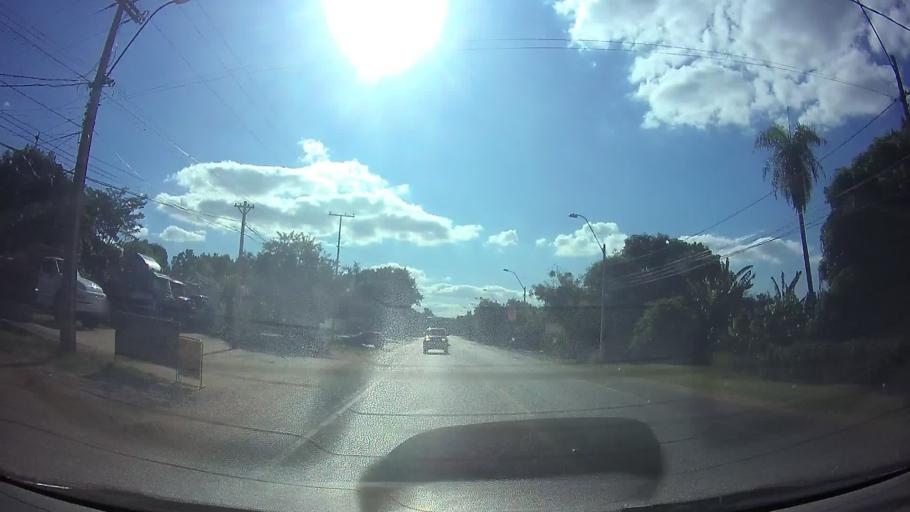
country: PY
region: Cordillera
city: Caacupe
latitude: -25.3895
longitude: -57.1577
